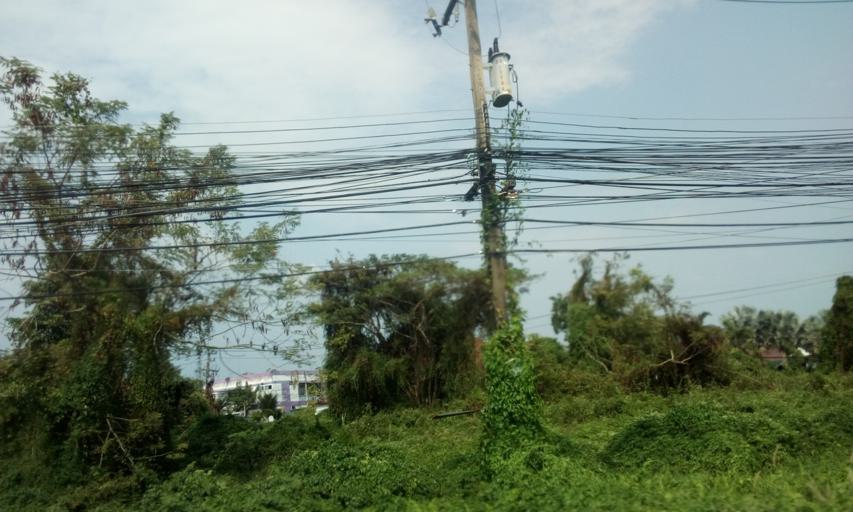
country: TH
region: Nakhon Nayok
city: Nakhon Nayok
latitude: 14.1994
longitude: 101.1931
